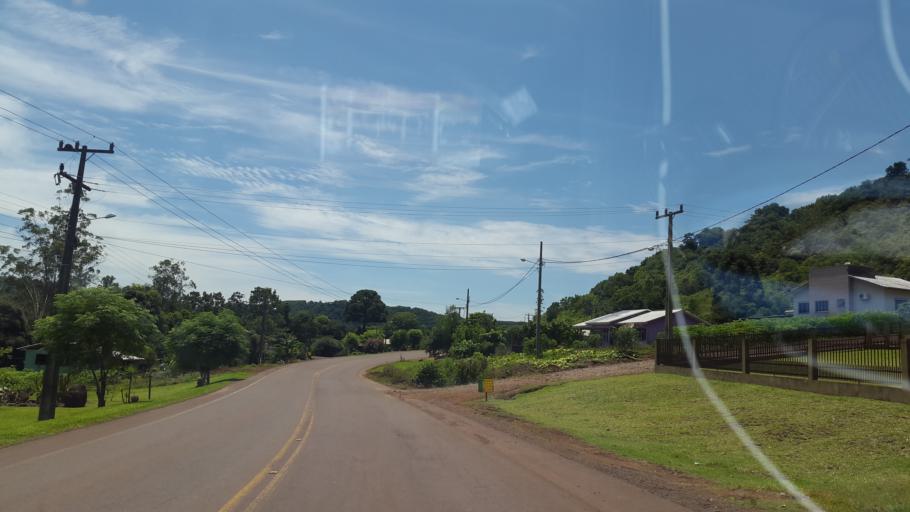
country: BR
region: Rio Grande do Sul
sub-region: Frederico Westphalen
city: Frederico Westphalen
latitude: -27.0742
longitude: -53.4244
